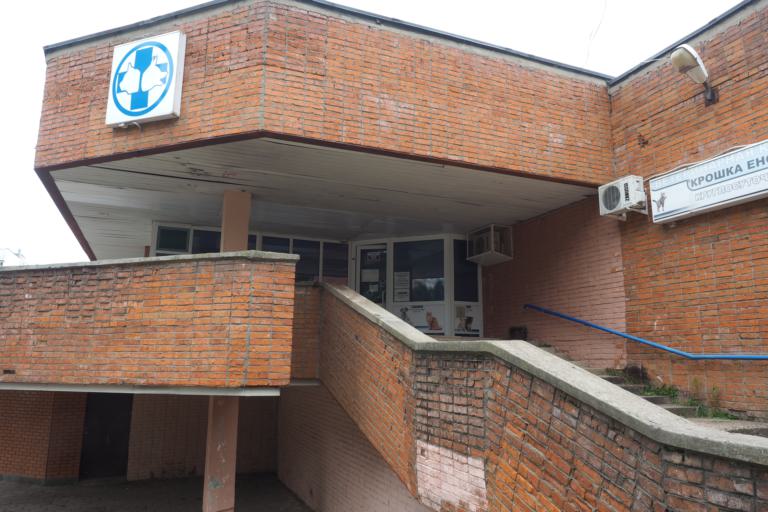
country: RU
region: Moskovskaya
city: Pushchino
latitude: 54.8293
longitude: 37.6376
